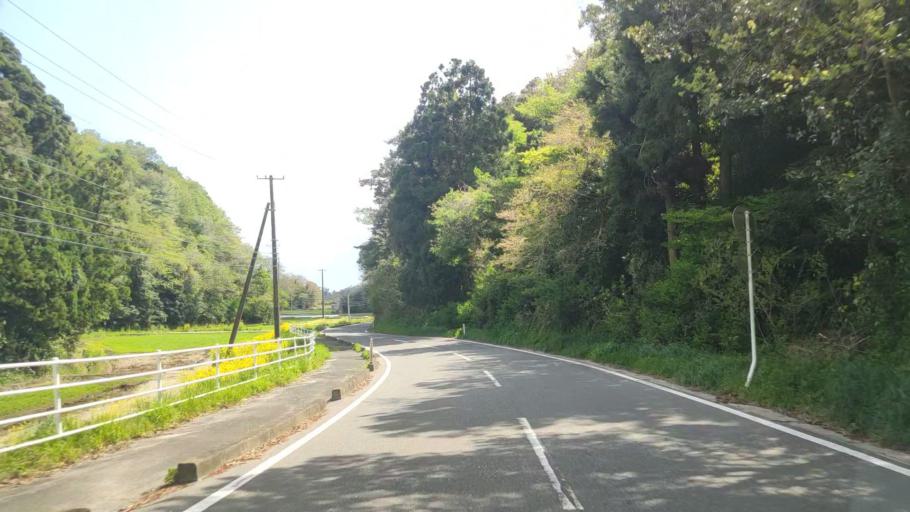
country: JP
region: Miyagi
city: Yamoto
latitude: 38.3330
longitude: 141.1628
